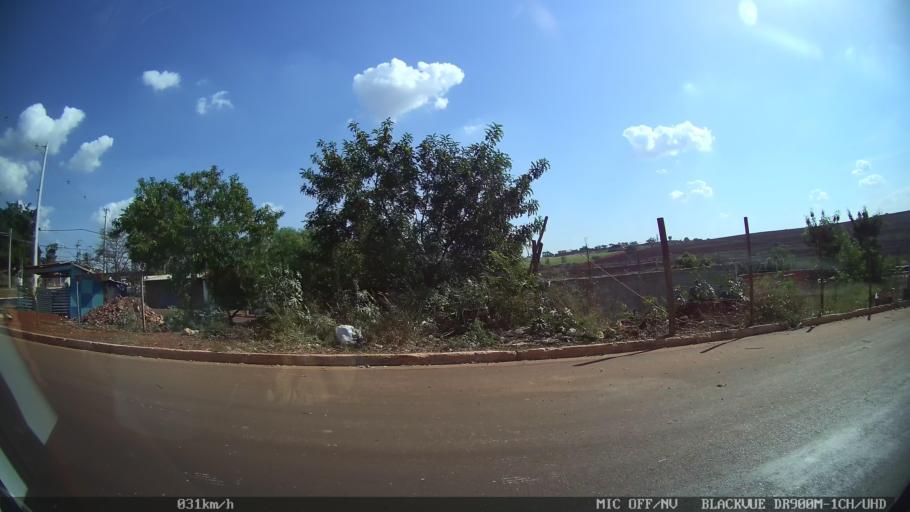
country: BR
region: Sao Paulo
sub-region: Ribeirao Preto
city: Ribeirao Preto
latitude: -21.1956
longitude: -47.8510
